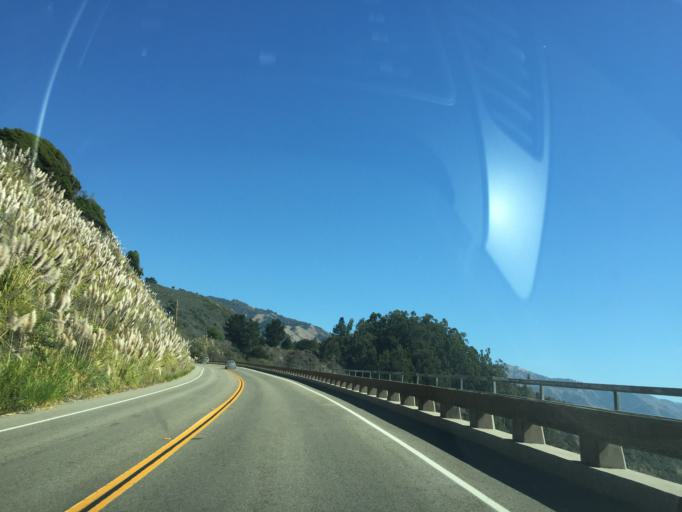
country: US
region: California
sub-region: Monterey County
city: Greenfield
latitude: 36.0205
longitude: -121.5462
